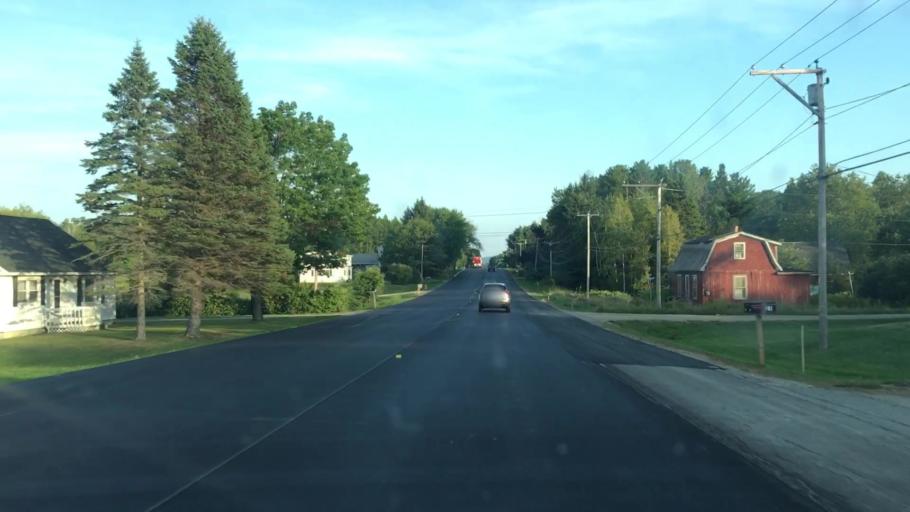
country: US
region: Maine
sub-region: Penobscot County
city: Hampden
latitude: 44.7648
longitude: -68.8522
